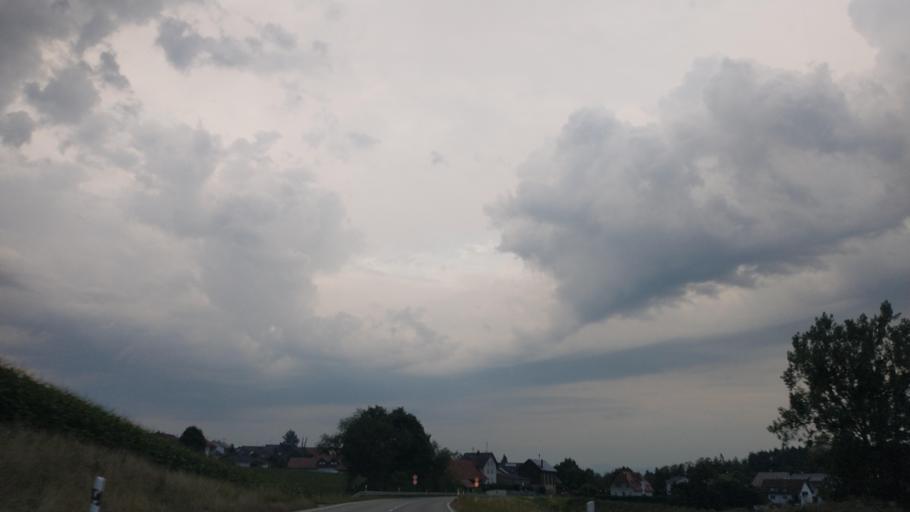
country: DE
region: Baden-Wuerttemberg
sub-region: Tuebingen Region
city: Tettnang
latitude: 47.6640
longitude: 9.6259
